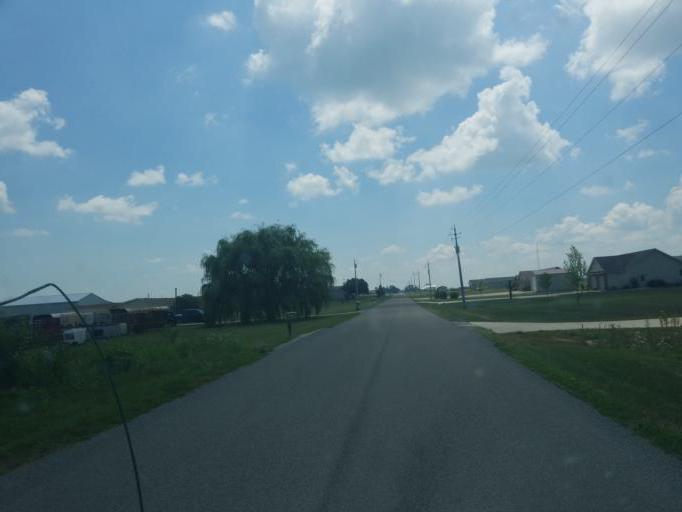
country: US
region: Ohio
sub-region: Mercer County
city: Celina
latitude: 40.5703
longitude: -84.4939
